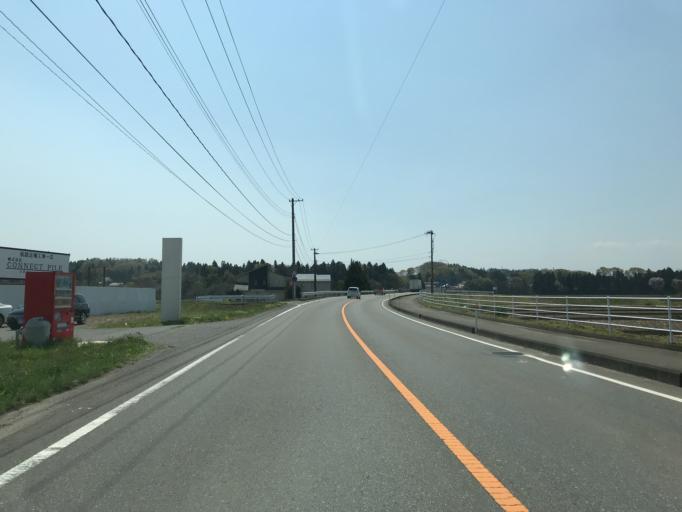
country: JP
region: Fukushima
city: Ishikawa
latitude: 37.1243
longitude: 140.3505
